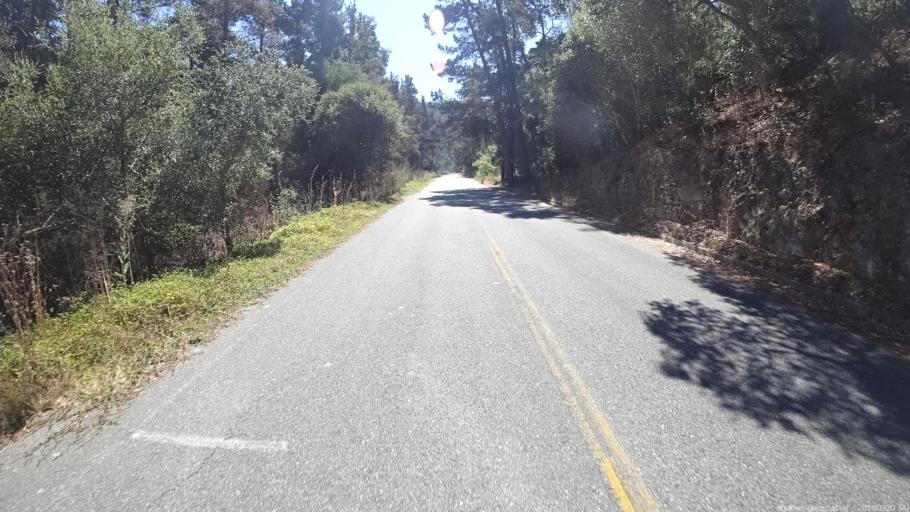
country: US
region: California
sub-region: Monterey County
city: Del Rey Oaks
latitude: 36.5717
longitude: -121.8562
